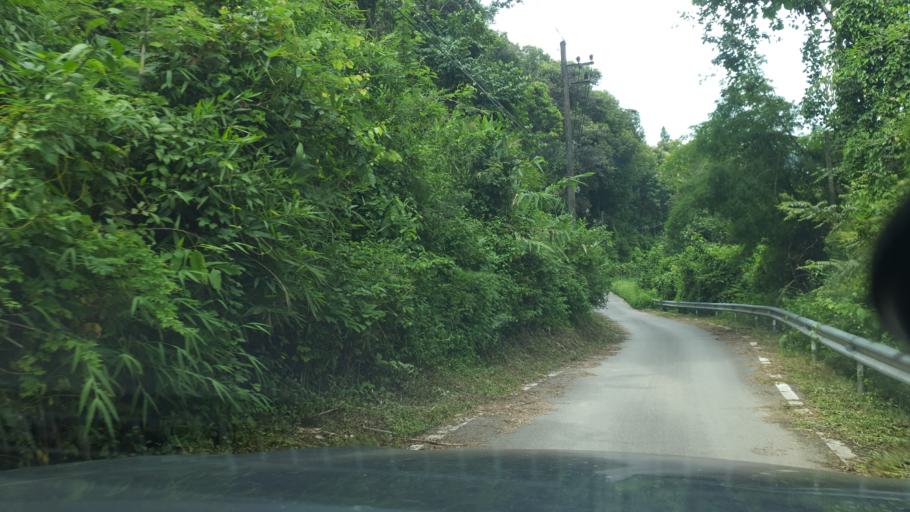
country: TH
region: Lamphun
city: Mae Tha
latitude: 18.5028
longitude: 99.2663
